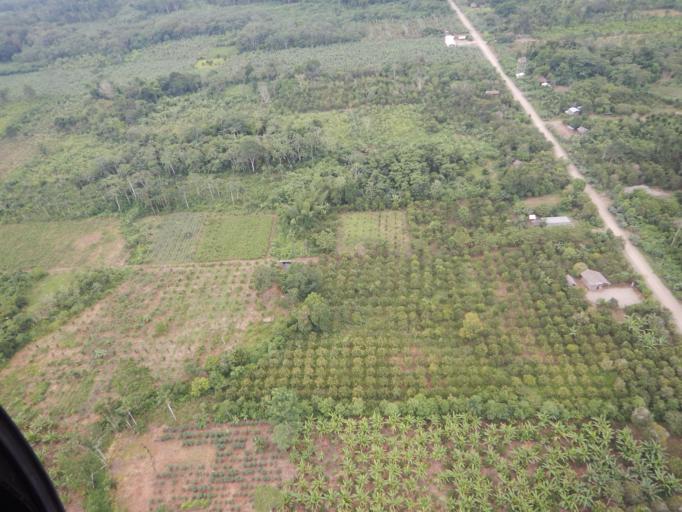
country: BO
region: Cochabamba
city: Chimore
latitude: -17.1934
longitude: -64.7378
